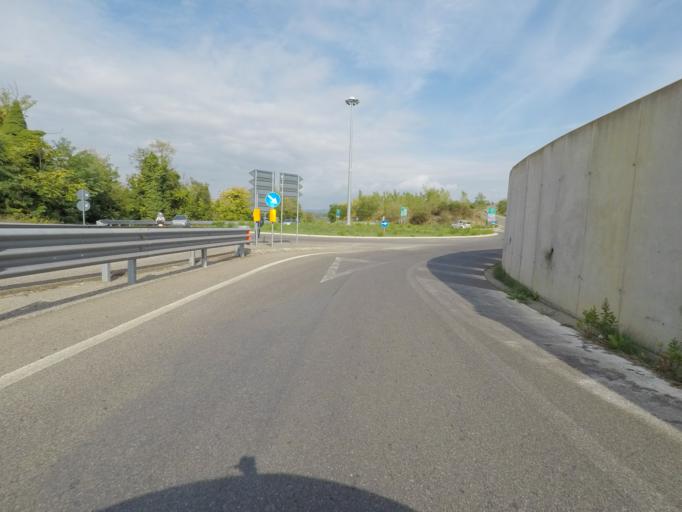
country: IT
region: Tuscany
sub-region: Provincia di Siena
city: Belverde
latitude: 43.3486
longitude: 11.3063
